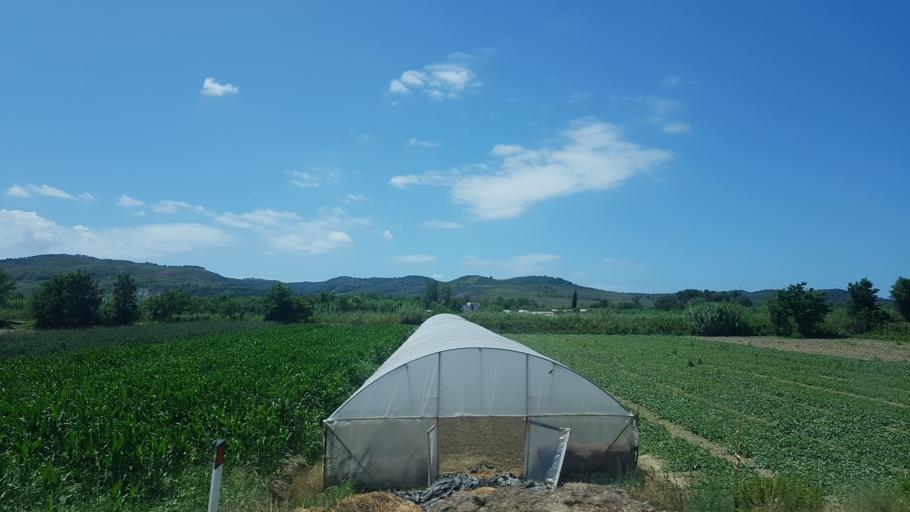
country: AL
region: Fier
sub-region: Rrethi i Fierit
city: Frakulla e Madhe
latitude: 40.6113
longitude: 19.5260
